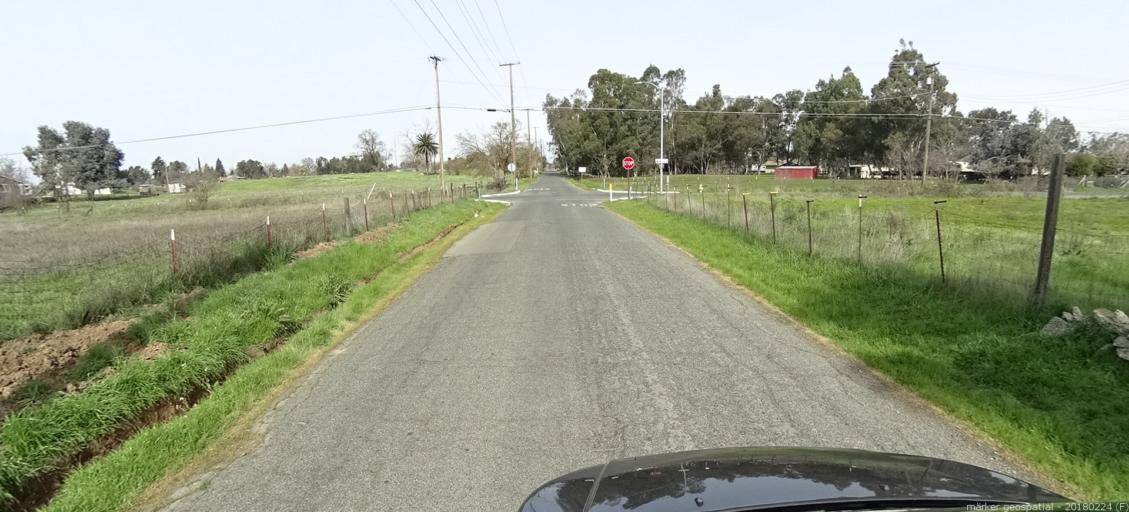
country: US
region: California
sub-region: Sacramento County
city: Rio Linda
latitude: 38.6909
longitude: -121.4708
